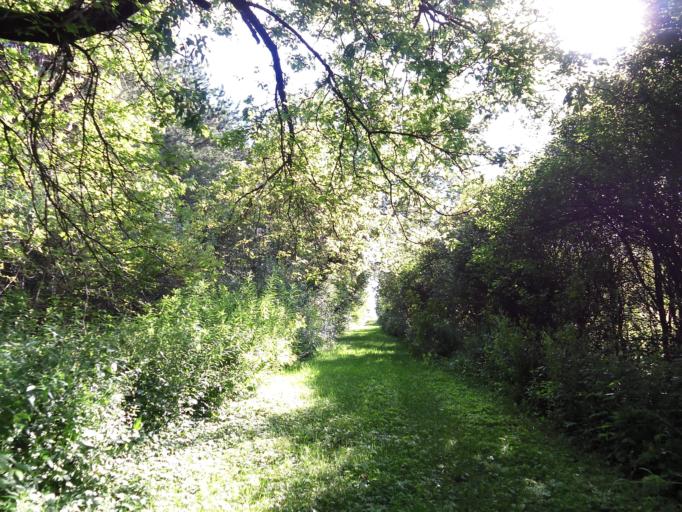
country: CA
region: Ontario
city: Bells Corners
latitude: 45.3128
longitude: -75.7373
